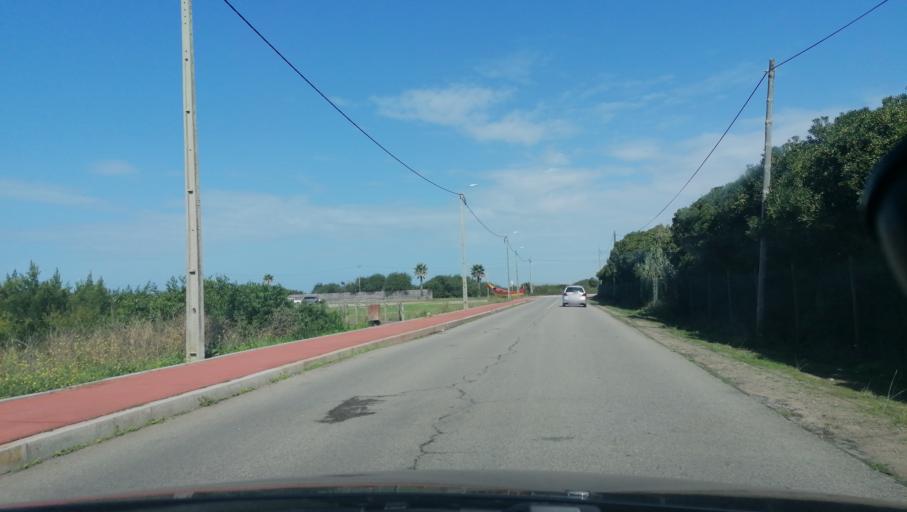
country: PT
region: Aveiro
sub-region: Espinho
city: Silvalde
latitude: 40.9880
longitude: -8.6443
